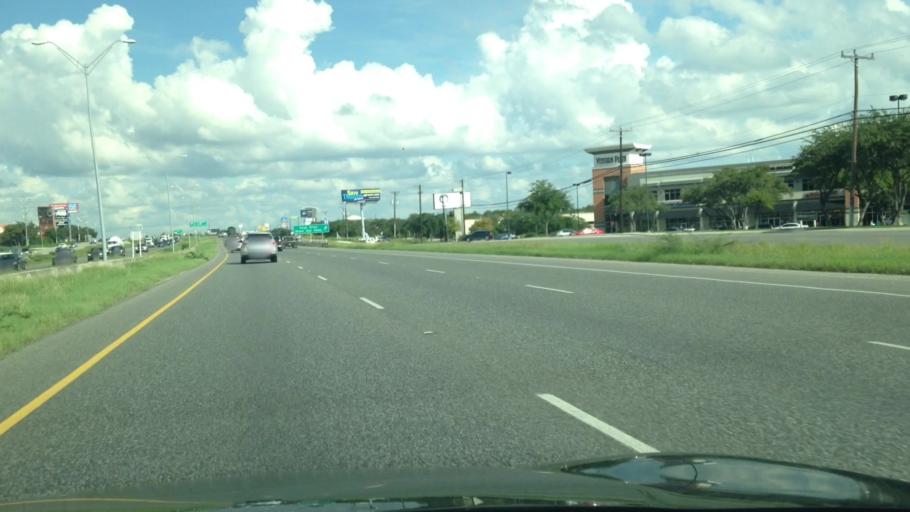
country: US
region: Texas
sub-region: Bexar County
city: Hollywood Park
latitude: 29.6082
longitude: -98.5022
